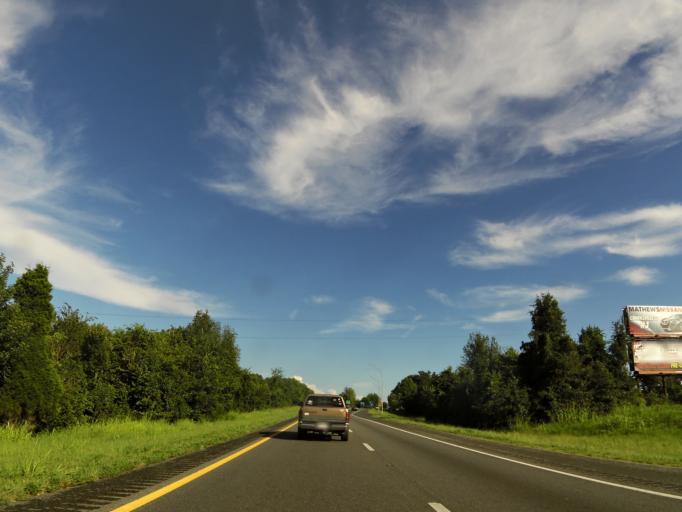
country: US
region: Tennessee
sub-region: Montgomery County
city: Clarksville
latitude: 36.5298
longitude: -87.2278
